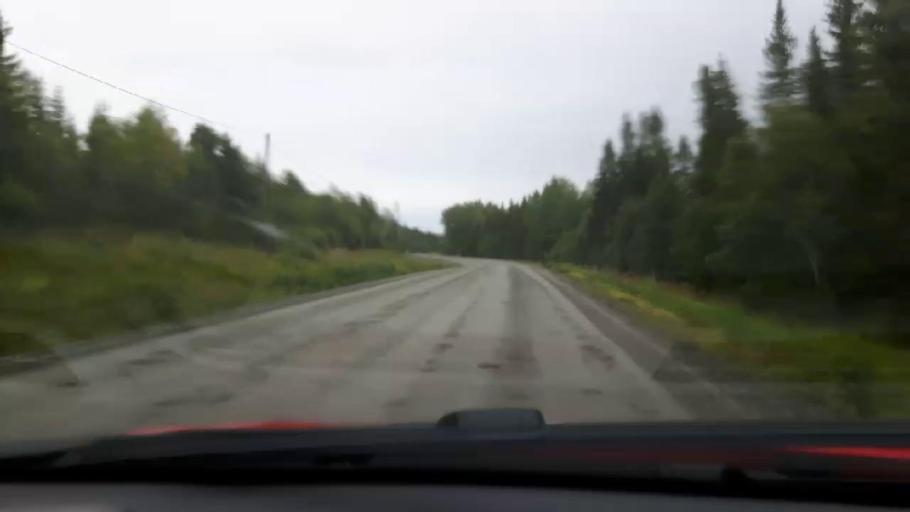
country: SE
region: Jaemtland
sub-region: Are Kommun
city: Are
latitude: 63.4550
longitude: 12.6455
